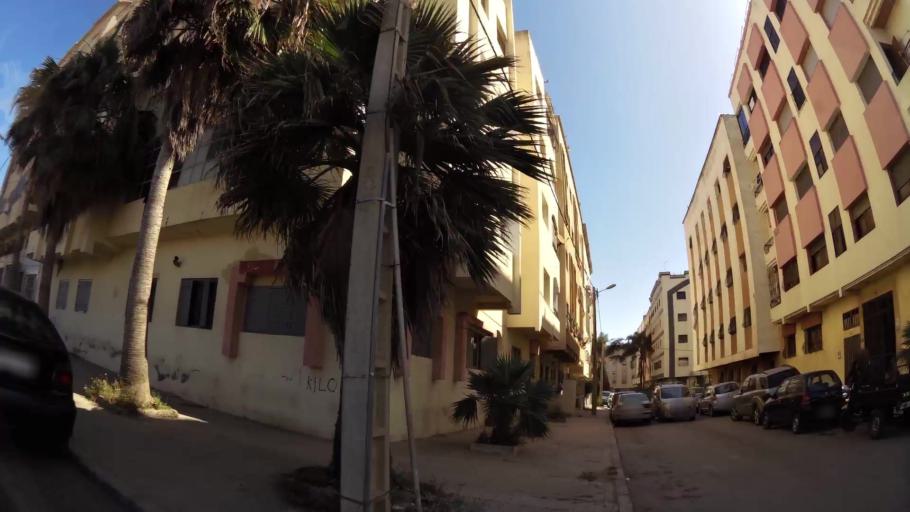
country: MA
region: Rabat-Sale-Zemmour-Zaer
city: Sale
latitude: 34.0674
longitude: -6.8020
